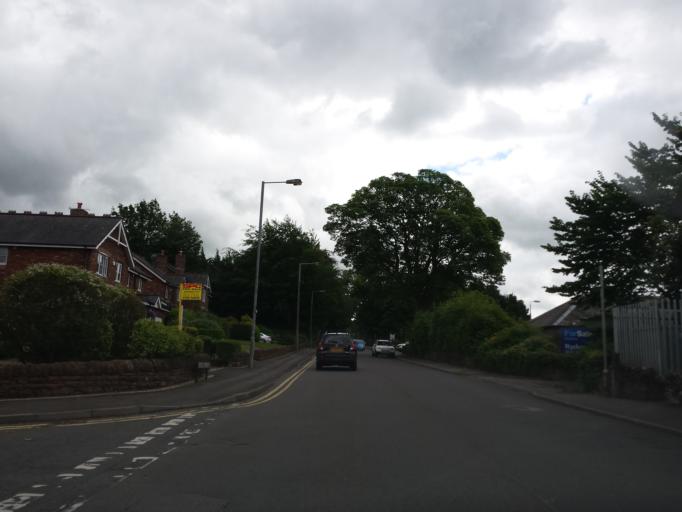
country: GB
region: Scotland
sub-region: Dumfries and Galloway
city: Dumfries
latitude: 55.0590
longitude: -3.5990
